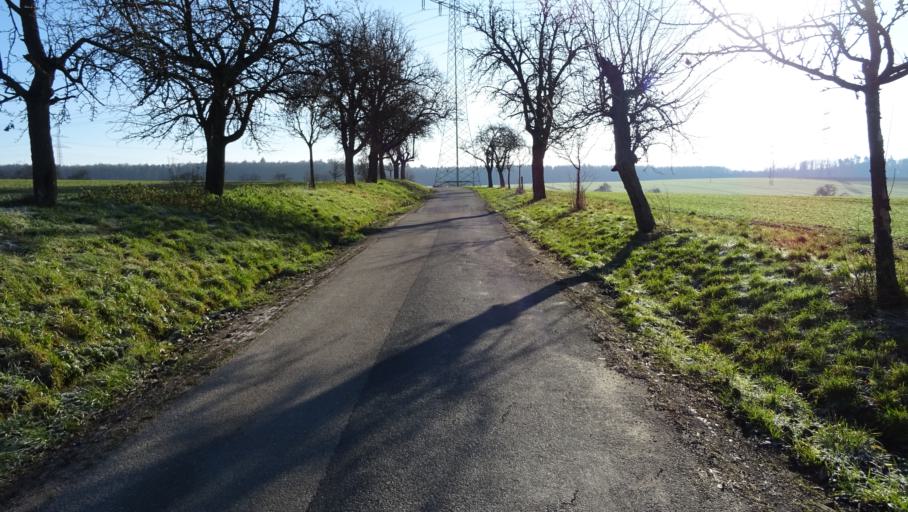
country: DE
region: Baden-Wuerttemberg
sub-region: Karlsruhe Region
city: Mosbach
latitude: 49.3438
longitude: 9.1814
